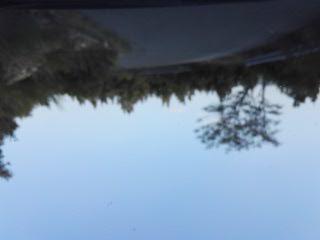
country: IT
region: Calabria
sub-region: Provincia di Vibo-Valentia
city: Nardodipace
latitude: 38.4344
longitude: 16.3437
